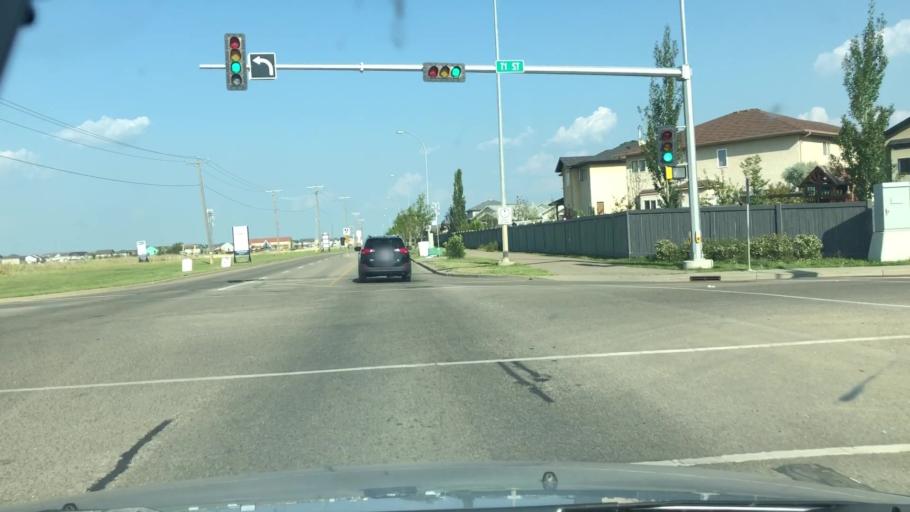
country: CA
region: Alberta
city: Edmonton
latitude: 53.6286
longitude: -113.4515
